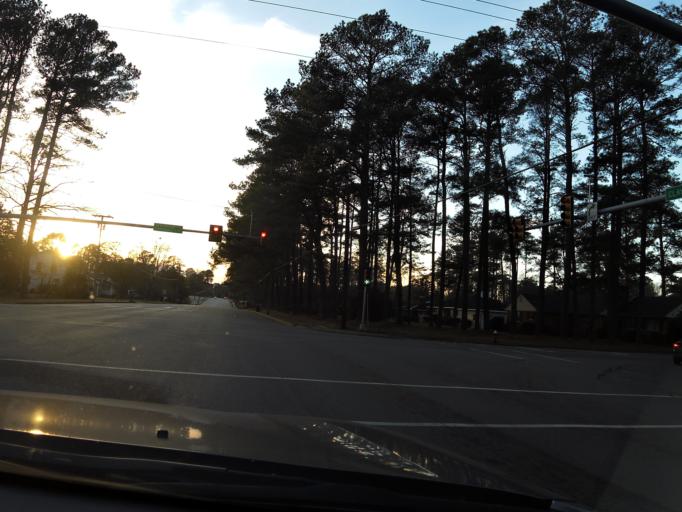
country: US
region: Virginia
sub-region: City of Franklin
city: Franklin
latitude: 36.6831
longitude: -76.9467
